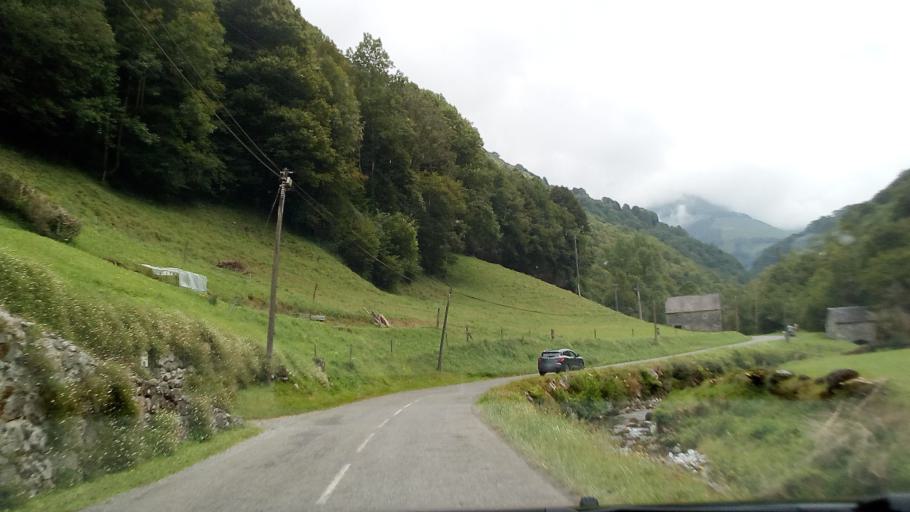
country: FR
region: Aquitaine
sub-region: Departement des Pyrenees-Atlantiques
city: Oloron-Sainte-Marie
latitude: 43.0777
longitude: -0.5962
